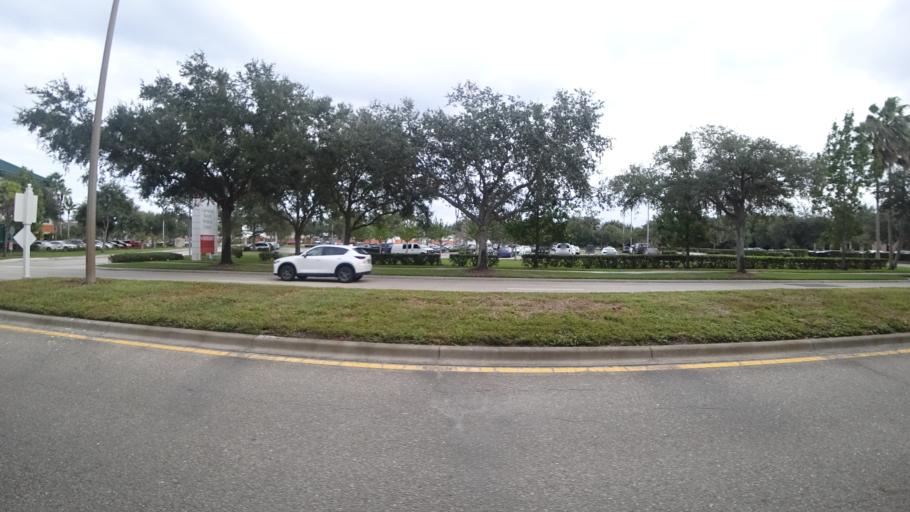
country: US
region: Florida
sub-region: Sarasota County
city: The Meadows
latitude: 27.3895
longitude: -82.4373
